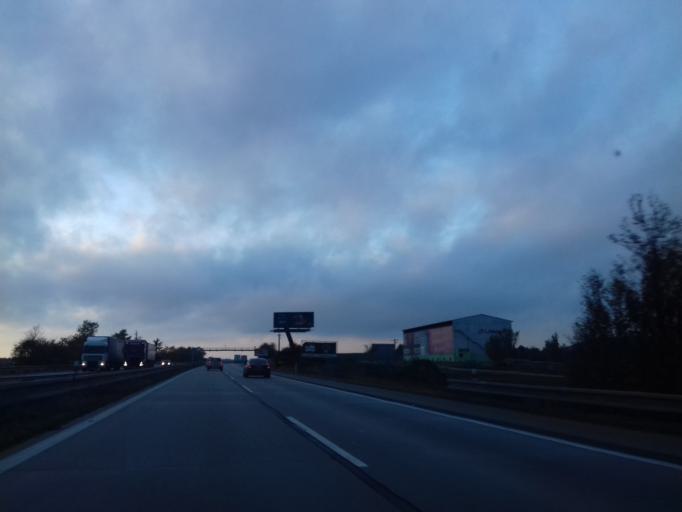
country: CZ
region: Vysocina
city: Krizanov
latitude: 49.3191
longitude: 16.0919
